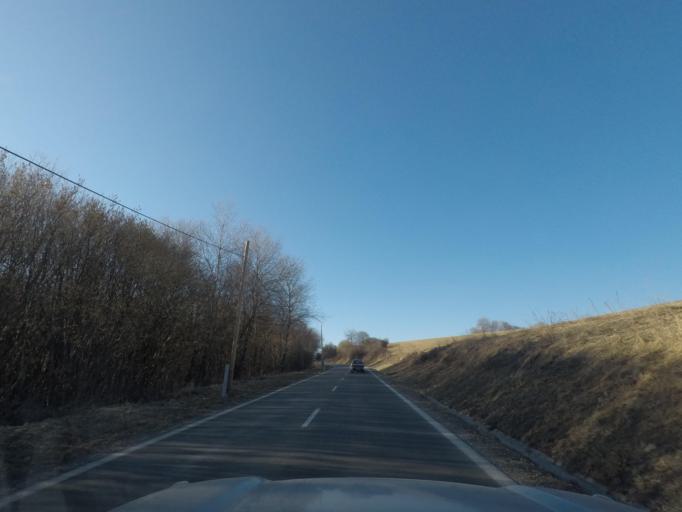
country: SK
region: Presovsky
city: Medzilaborce
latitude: 49.2069
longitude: 21.9878
